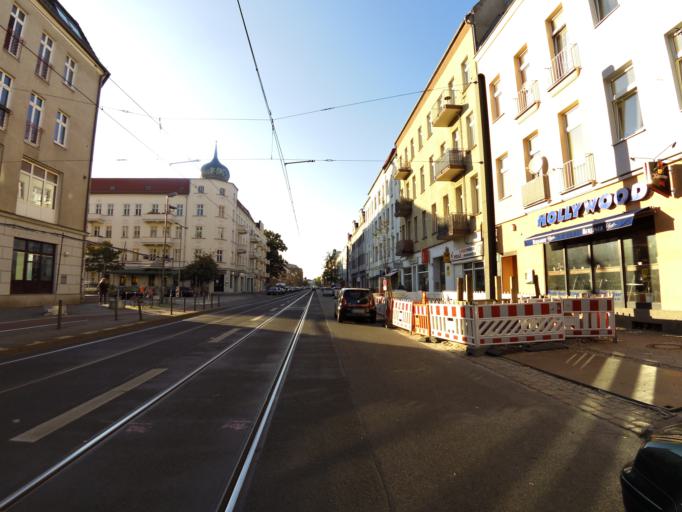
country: DE
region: Berlin
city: Oberschoneweide
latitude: 52.4612
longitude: 13.5197
